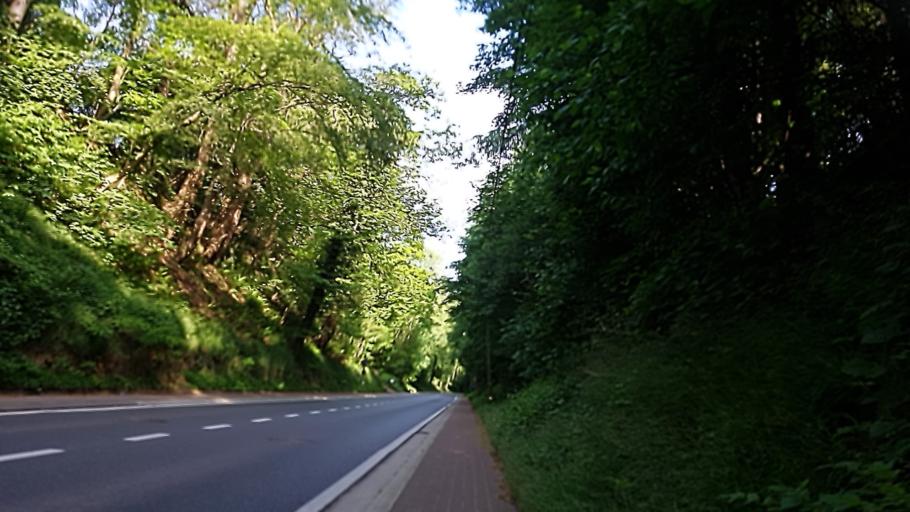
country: BE
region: Flanders
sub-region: Provincie Vlaams-Brabant
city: Overijse
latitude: 50.7681
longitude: 4.5475
